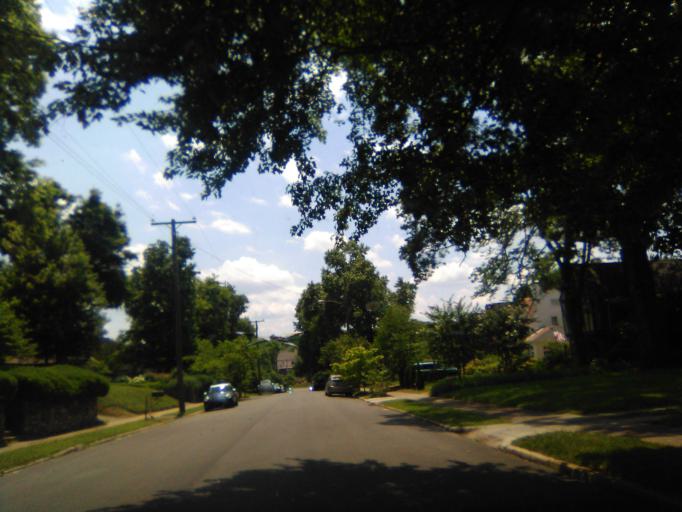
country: US
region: Tennessee
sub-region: Davidson County
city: Belle Meade
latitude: 36.1301
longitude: -86.8290
